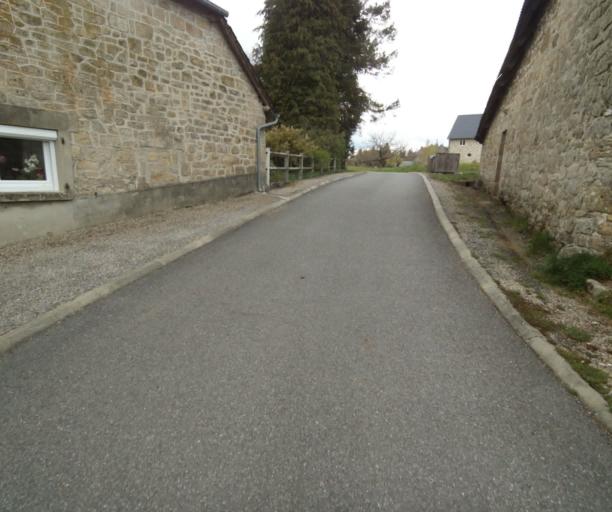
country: FR
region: Limousin
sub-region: Departement de la Correze
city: Correze
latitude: 45.2959
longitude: 1.9194
